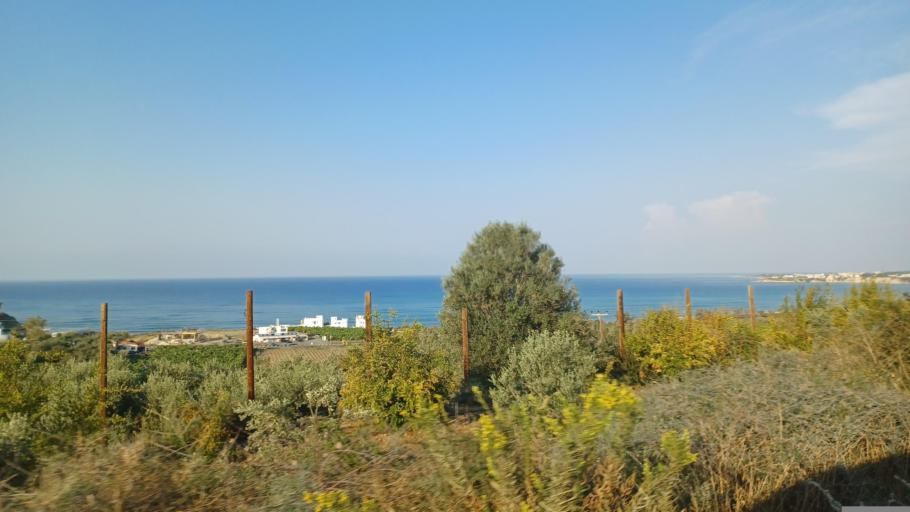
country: CY
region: Pafos
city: Kissonerga
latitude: 34.8332
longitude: 32.3967
